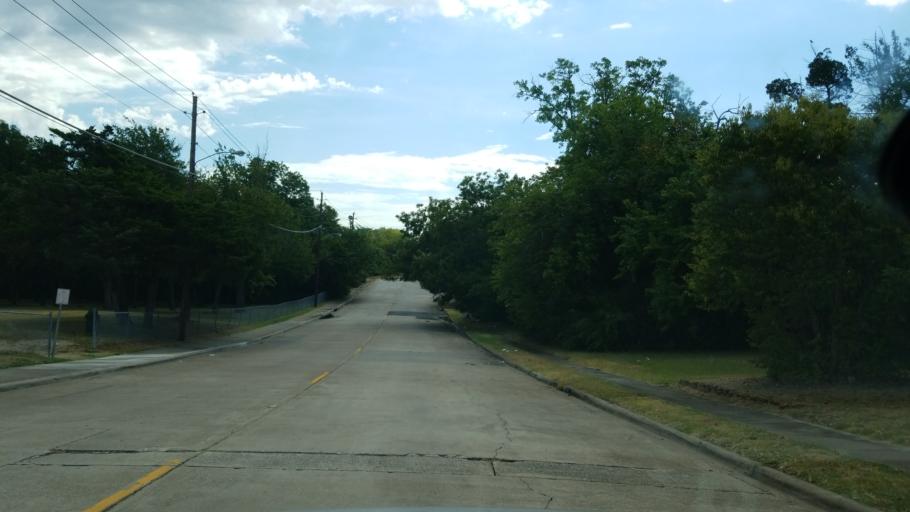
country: US
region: Texas
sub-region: Dallas County
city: Duncanville
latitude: 32.6549
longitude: -96.8471
